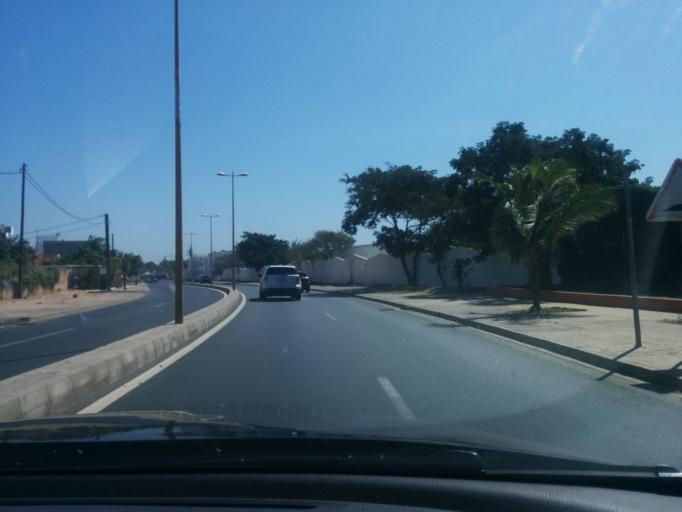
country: SN
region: Dakar
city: Mermoz Boabab
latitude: 14.7024
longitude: -17.4783
